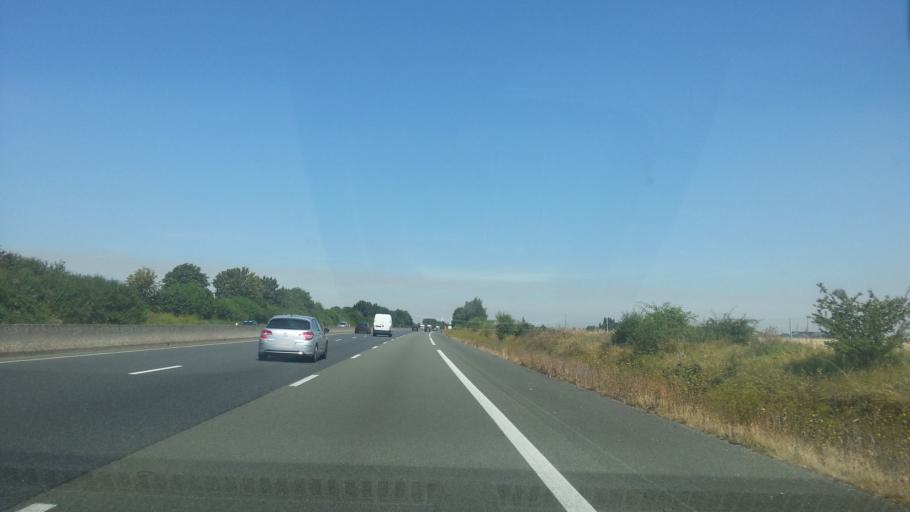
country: FR
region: Centre
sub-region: Departement d'Eure-et-Loir
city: Janville
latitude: 48.2169
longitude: 1.8470
